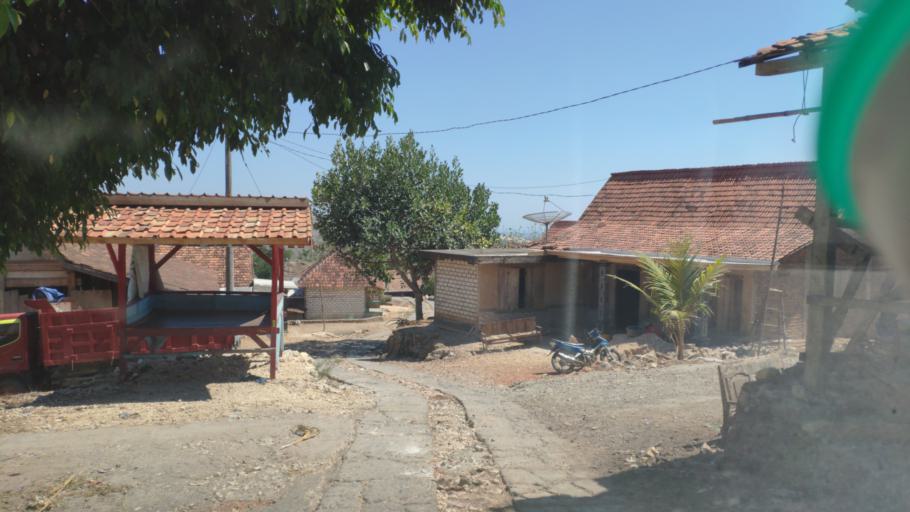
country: ID
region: Central Java
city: Jurangjero
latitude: -6.8949
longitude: 111.5093
